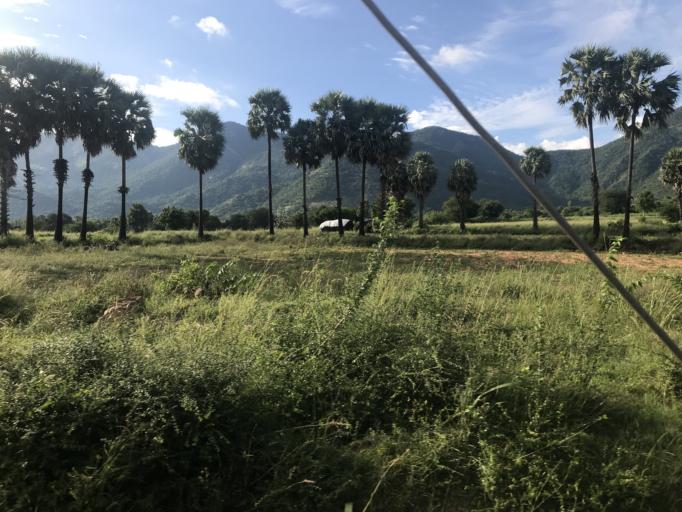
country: IN
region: Tamil Nadu
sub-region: Coimbatore
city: Madukkarai
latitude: 10.8888
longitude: 76.8791
